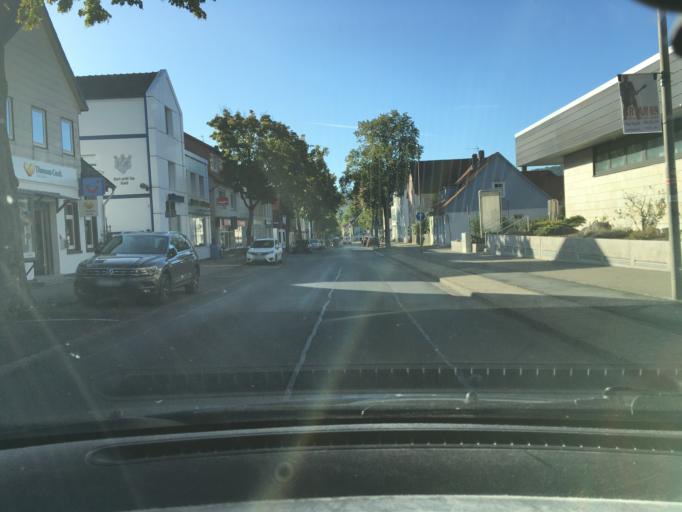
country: DE
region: Lower Saxony
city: Springe
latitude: 52.2116
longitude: 9.5578
